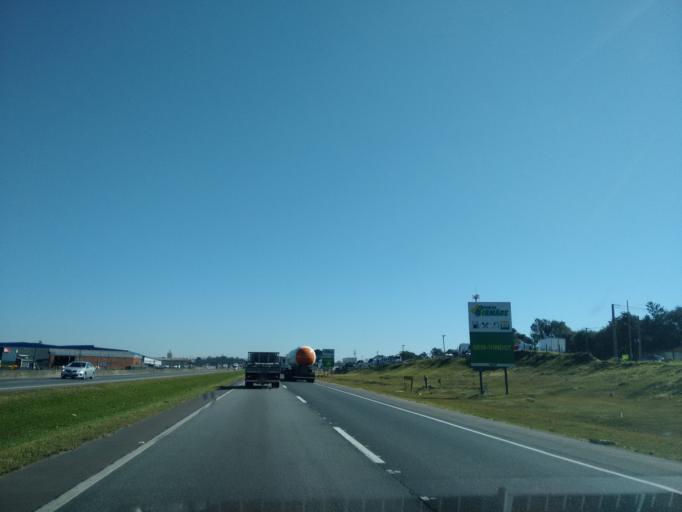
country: BR
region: Parana
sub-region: Sao Jose Dos Pinhais
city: Sao Jose dos Pinhais
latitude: -25.5525
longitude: -49.2779
